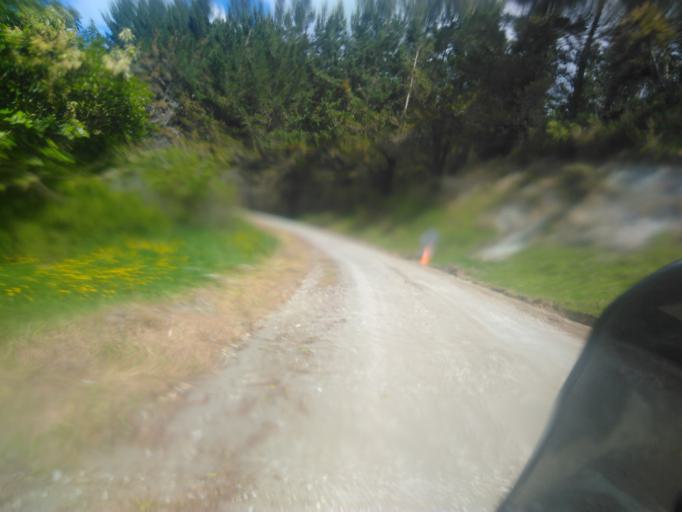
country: NZ
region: Hawke's Bay
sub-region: Wairoa District
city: Wairoa
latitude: -38.7746
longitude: 177.6061
